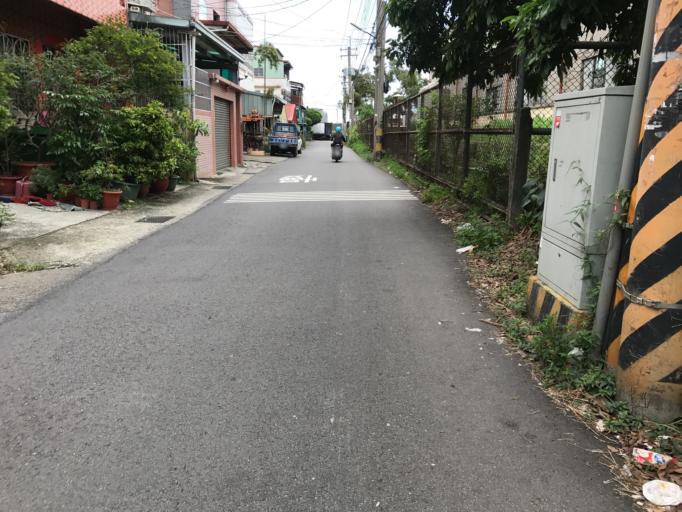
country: TW
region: Taiwan
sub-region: Taichung City
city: Taichung
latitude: 24.0785
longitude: 120.7132
